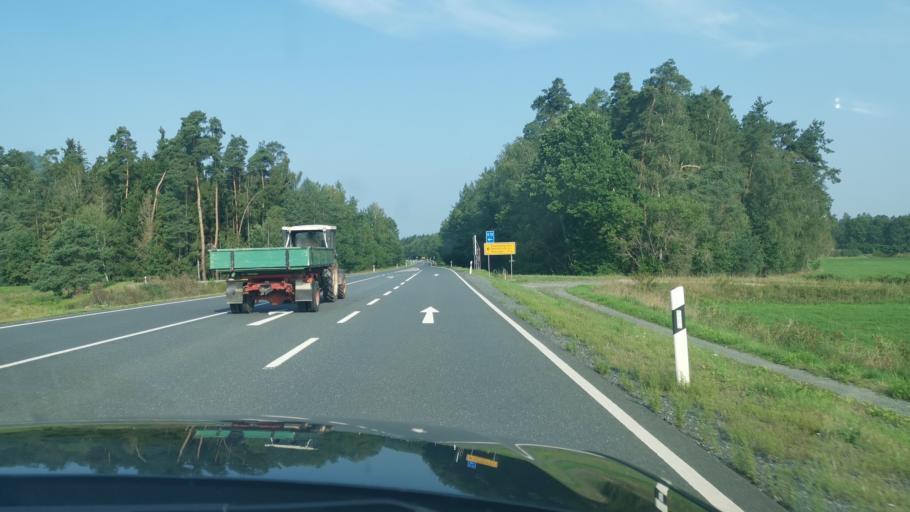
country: DE
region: Bavaria
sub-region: Upper Palatinate
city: Wernberg-Koblitz
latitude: 49.5364
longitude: 12.1249
